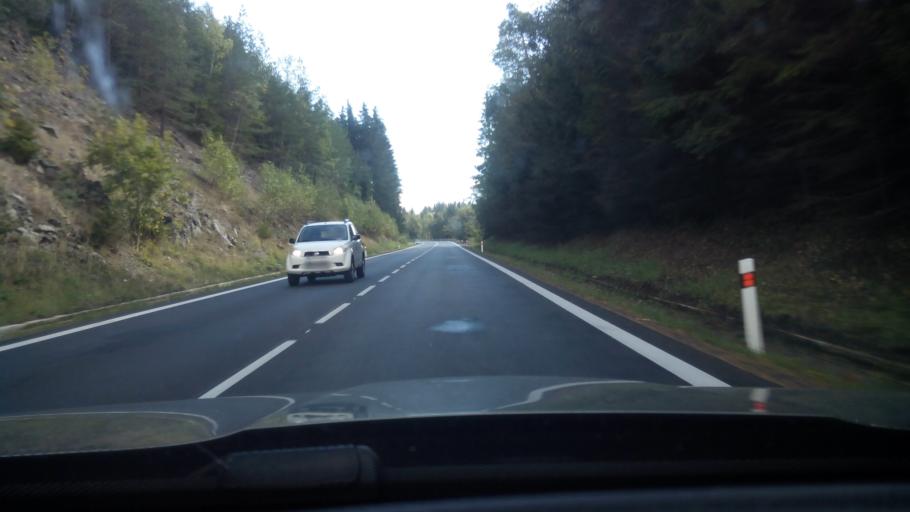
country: CZ
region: Jihocesky
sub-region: Okres Prachatice
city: Zdikov
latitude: 49.0704
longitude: 13.7154
